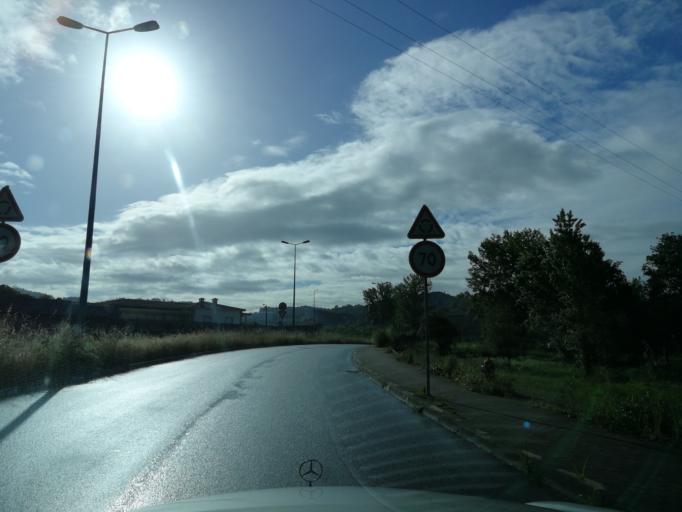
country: PT
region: Braga
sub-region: Braga
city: Braga
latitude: 41.5661
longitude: -8.4409
